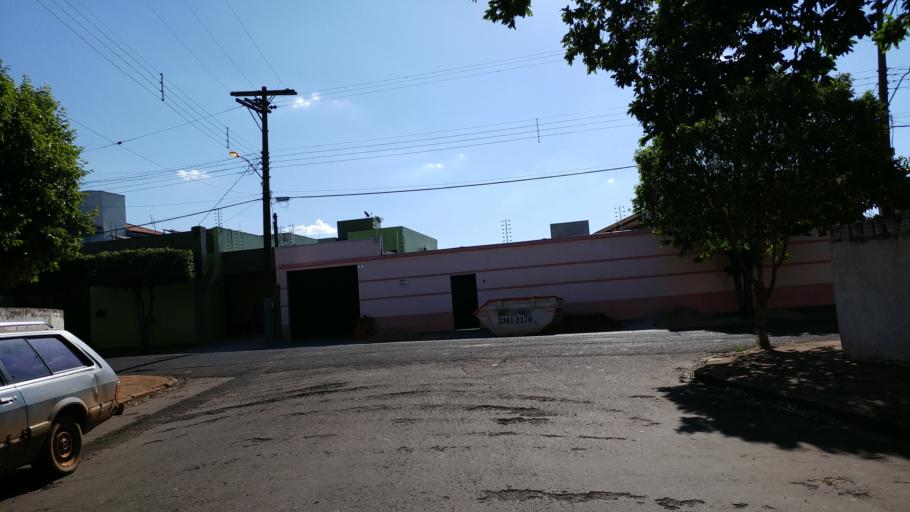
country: BR
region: Sao Paulo
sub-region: Paraguacu Paulista
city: Paraguacu Paulista
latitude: -22.4257
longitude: -50.5791
